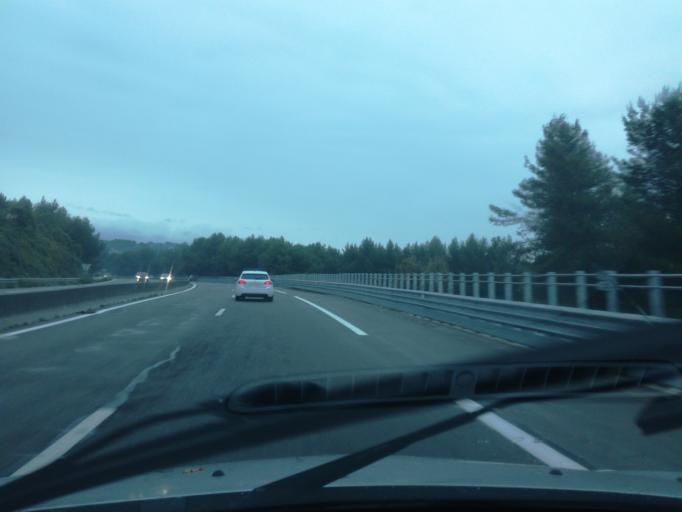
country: FR
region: Provence-Alpes-Cote d'Azur
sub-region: Departement des Alpes-Maritimes
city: Mougins
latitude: 43.6020
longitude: 7.0026
